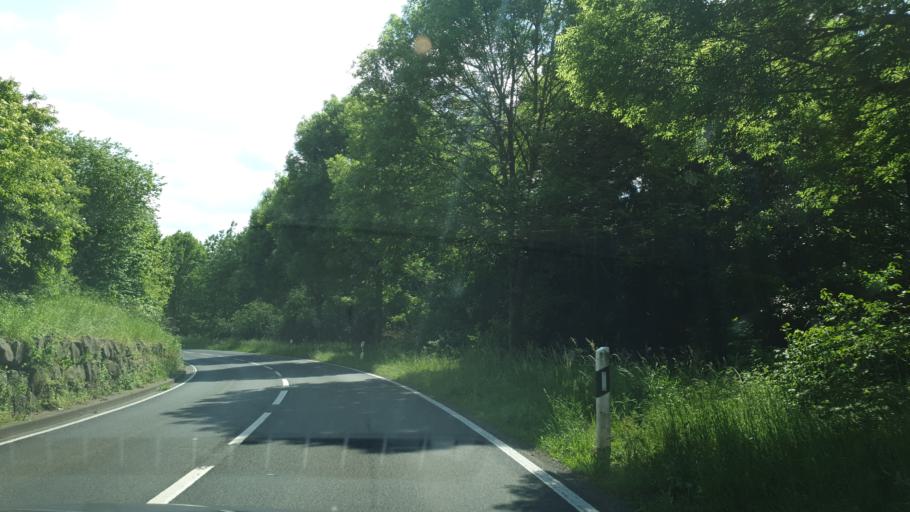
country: DE
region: Rheinland-Pfalz
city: Mogendorf
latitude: 50.4879
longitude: 7.7795
